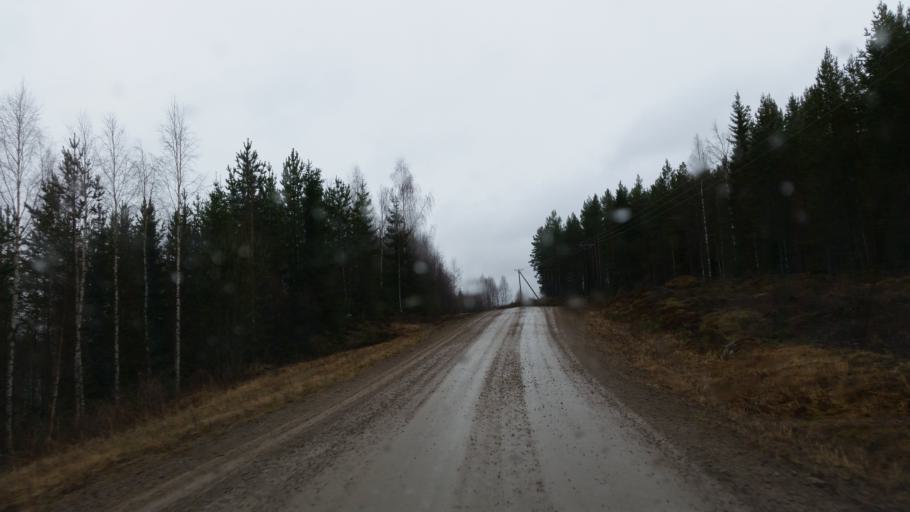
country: SE
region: Vaesternorrland
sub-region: Ange Kommun
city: Ange
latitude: 62.1569
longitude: 15.6625
